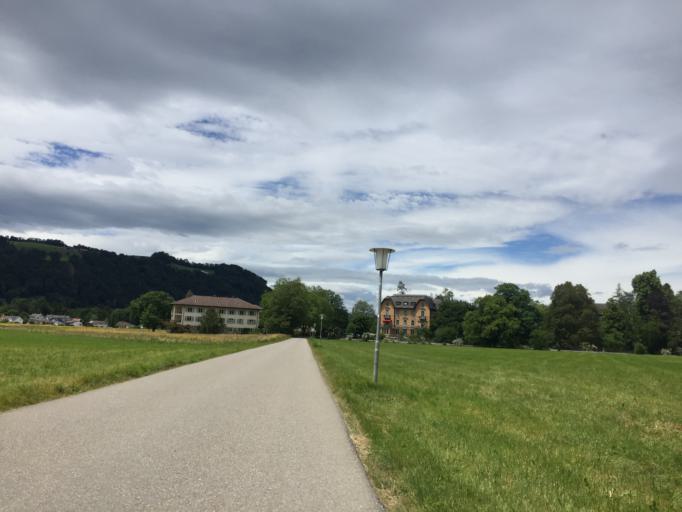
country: CH
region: Bern
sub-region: Bern-Mittelland District
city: Munsingen
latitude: 46.8782
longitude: 7.5552
